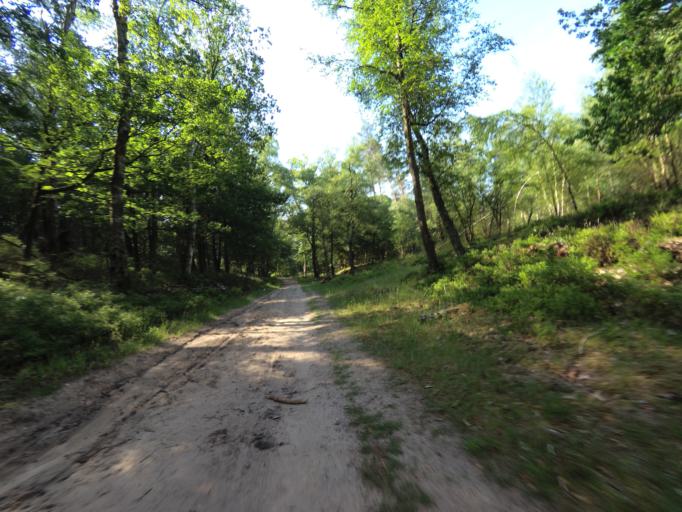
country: NL
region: Gelderland
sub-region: Gemeente Apeldoorn
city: Beekbergen
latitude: 52.1556
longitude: 5.9016
